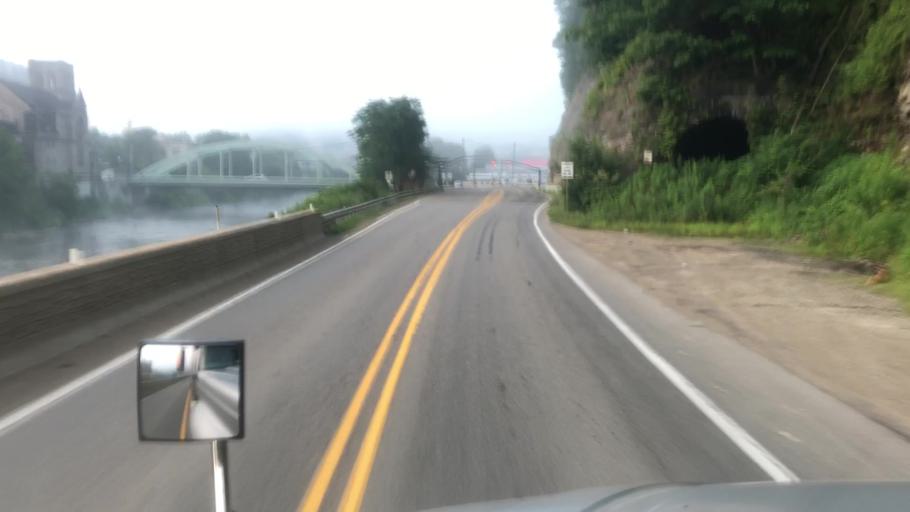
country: US
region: Pennsylvania
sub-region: Venango County
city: Oil City
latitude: 41.4356
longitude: -79.7103
